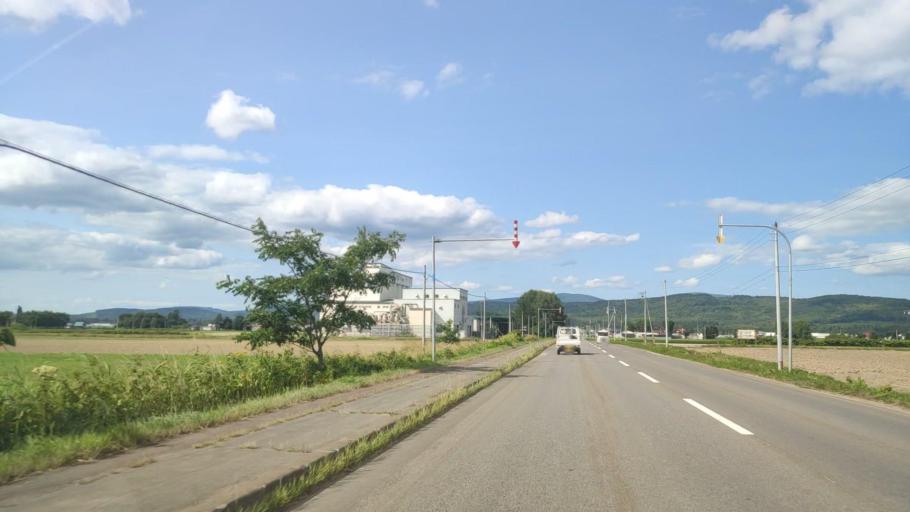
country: JP
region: Hokkaido
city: Nayoro
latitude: 44.4309
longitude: 142.4008
